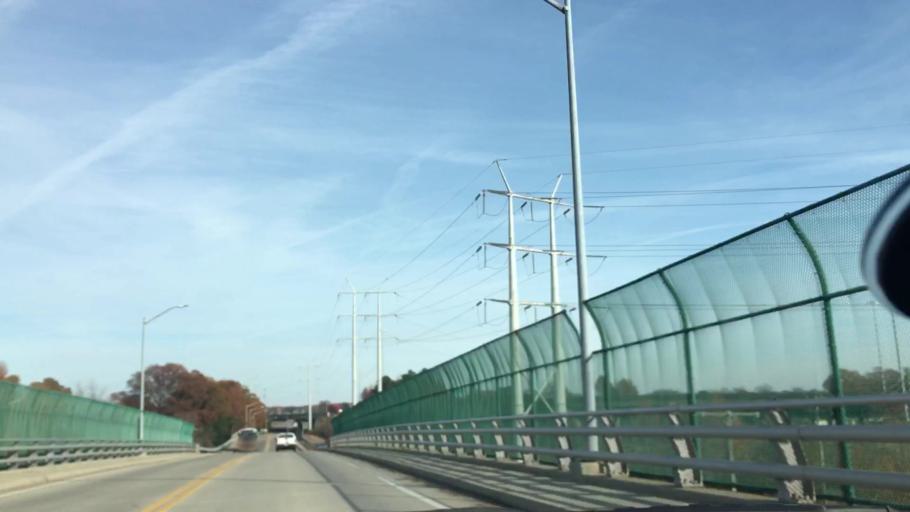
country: US
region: Virginia
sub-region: City of Newport News
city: Newport News
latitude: 36.9896
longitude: -76.4292
